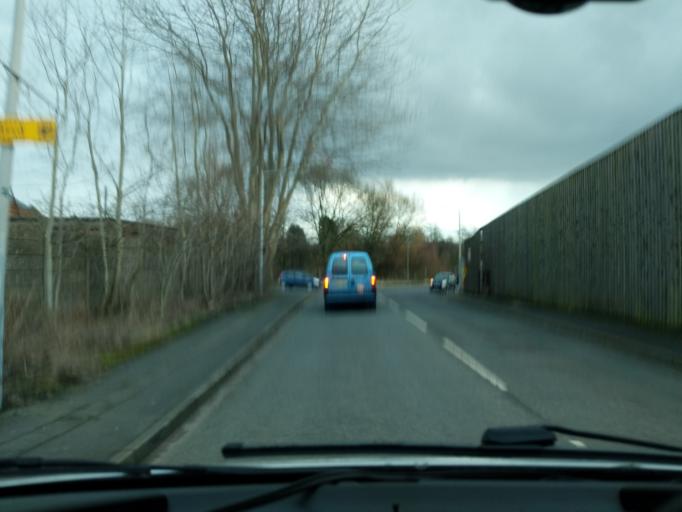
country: GB
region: England
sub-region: St. Helens
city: St Helens
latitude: 53.4396
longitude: -2.7070
